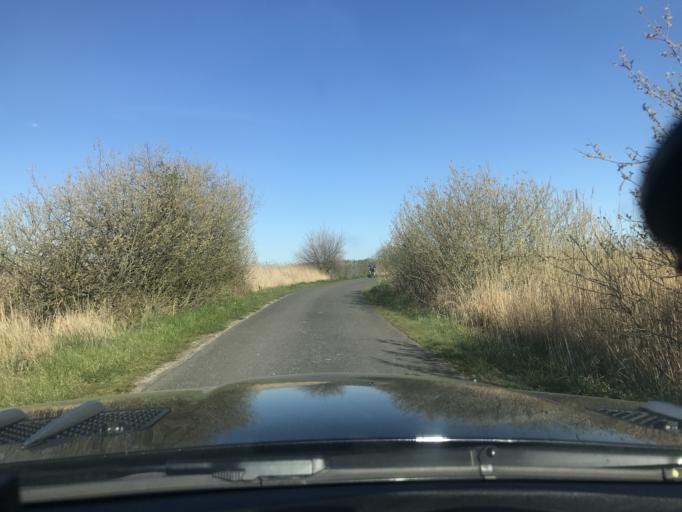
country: DE
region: Schleswig-Holstein
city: Heiligenhafen
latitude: 54.4655
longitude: 11.0155
